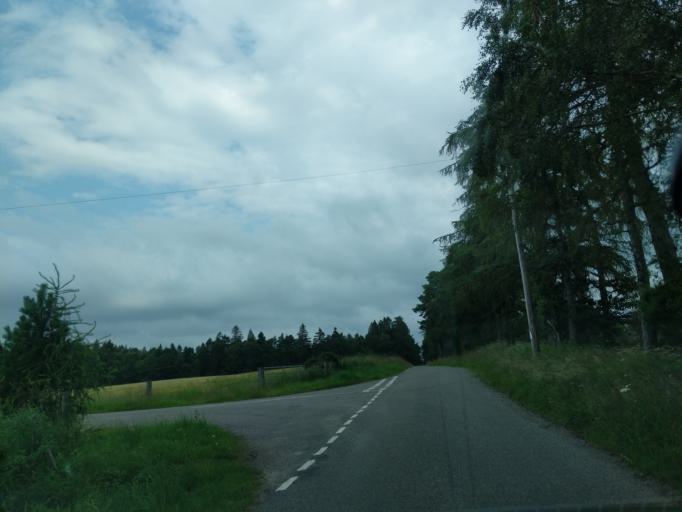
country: GB
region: Scotland
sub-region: Moray
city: Rothes
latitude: 57.4804
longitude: -3.2350
